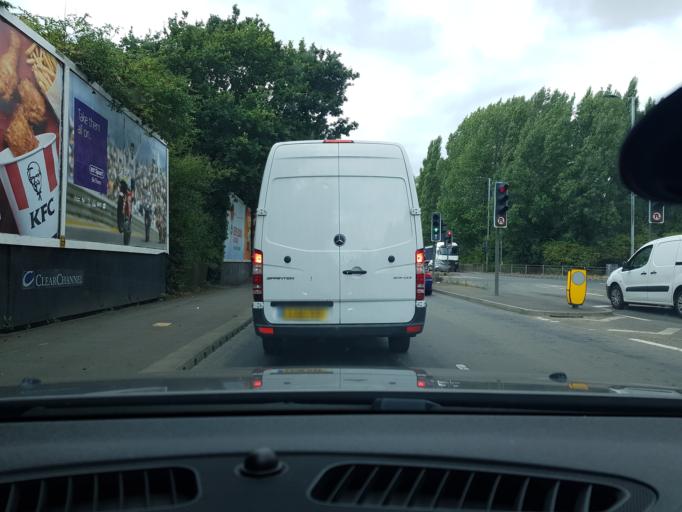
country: GB
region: England
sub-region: Surrey
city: Colnbrook
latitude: 51.4844
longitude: -0.5089
